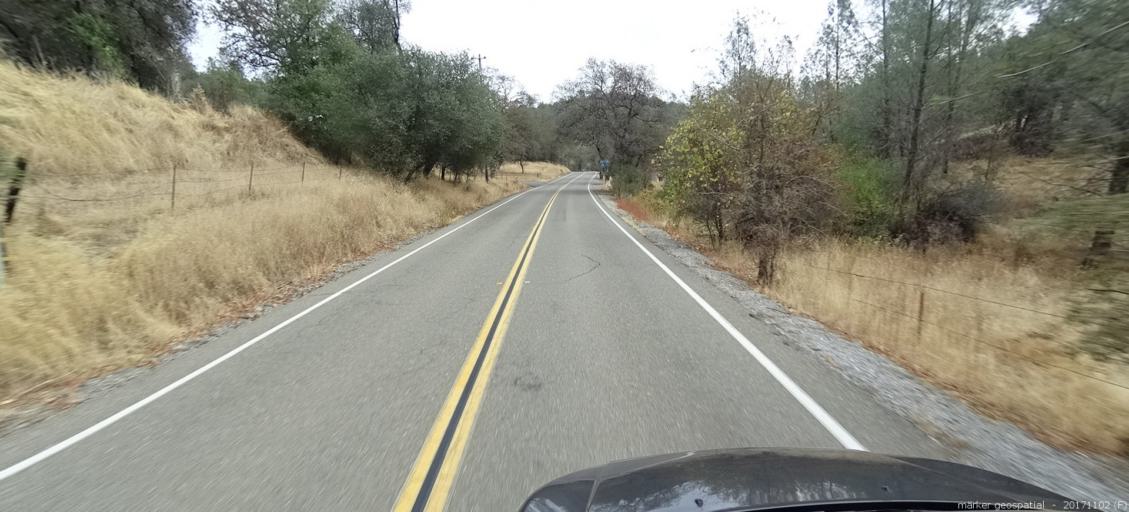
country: US
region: California
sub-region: Shasta County
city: Bella Vista
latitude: 40.7032
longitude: -122.2612
